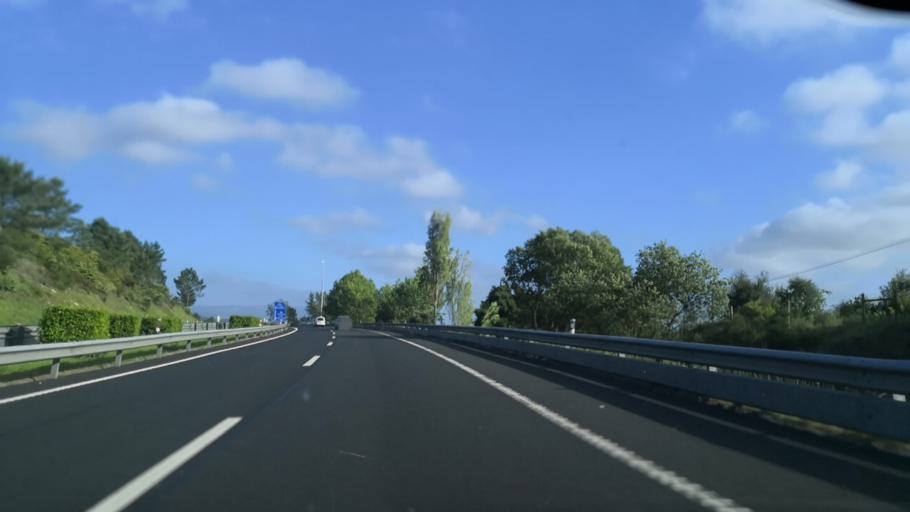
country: PT
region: Leiria
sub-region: Bombarral
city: Bombarral
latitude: 39.2987
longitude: -9.1631
